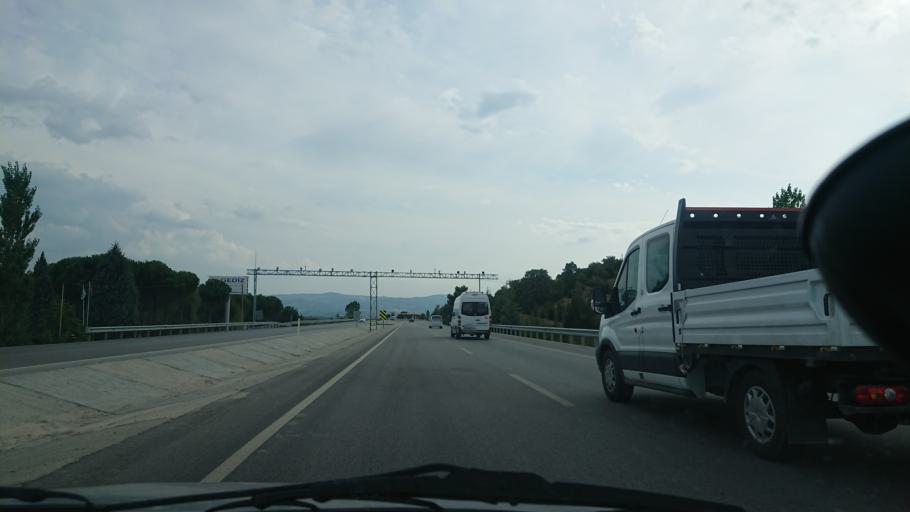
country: TR
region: Kuetahya
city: Gediz
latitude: 39.0135
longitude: 29.4094
